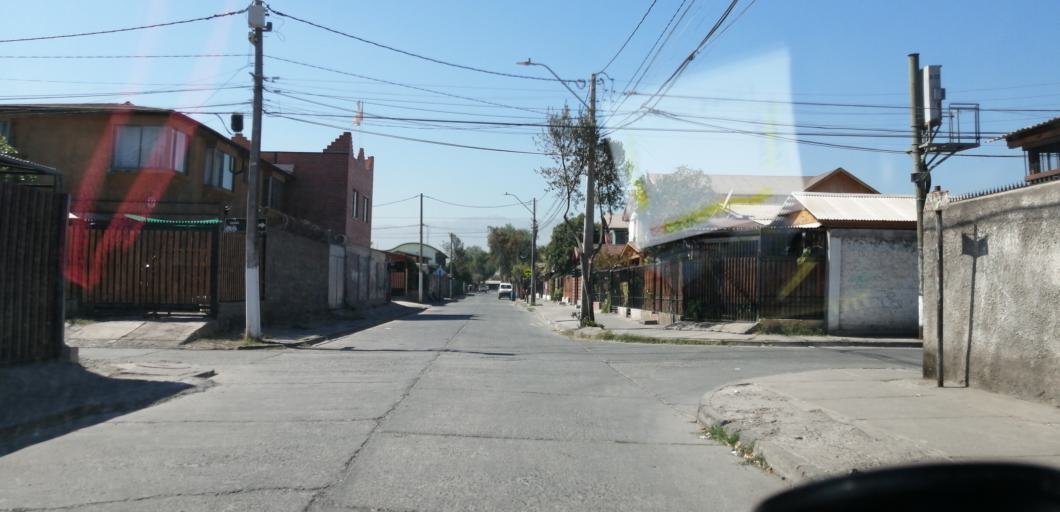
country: CL
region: Santiago Metropolitan
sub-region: Provincia de Santiago
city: Lo Prado
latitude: -33.4342
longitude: -70.7565
